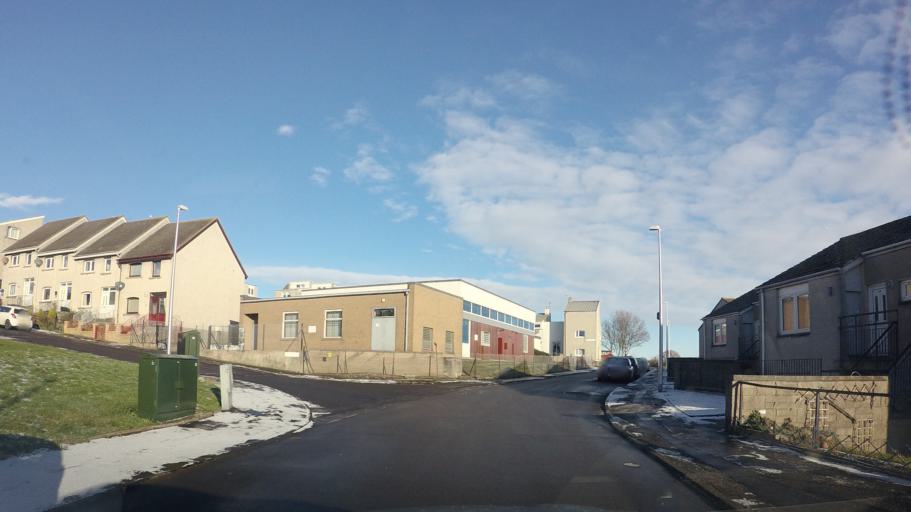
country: GB
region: Scotland
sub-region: Fife
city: Inverkeithing
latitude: 56.0312
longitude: -3.3996
